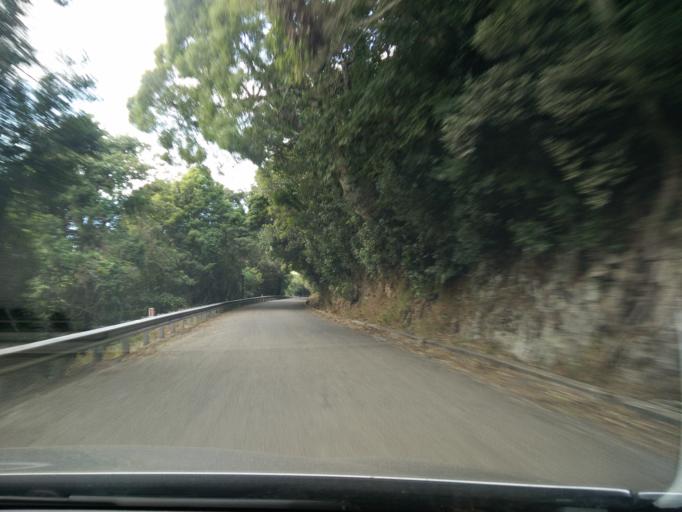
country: AU
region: New South Wales
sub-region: Kiama
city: Jamberoo
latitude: -34.6980
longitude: 150.7954
